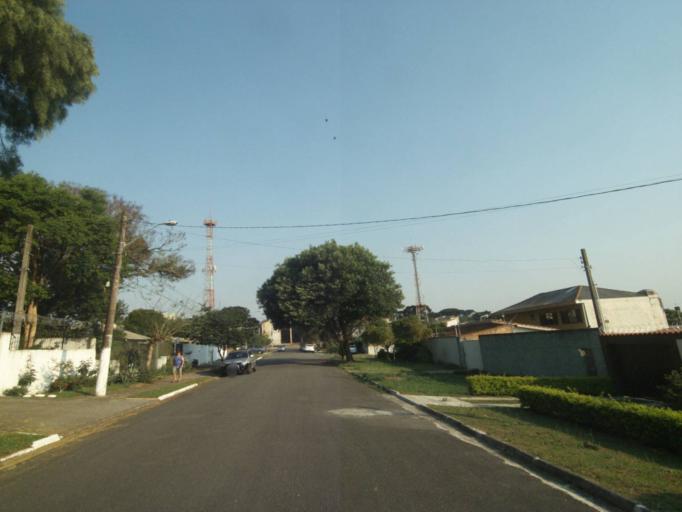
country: BR
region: Parana
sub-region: Sao Jose Dos Pinhais
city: Sao Jose dos Pinhais
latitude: -25.5256
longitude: -49.2549
